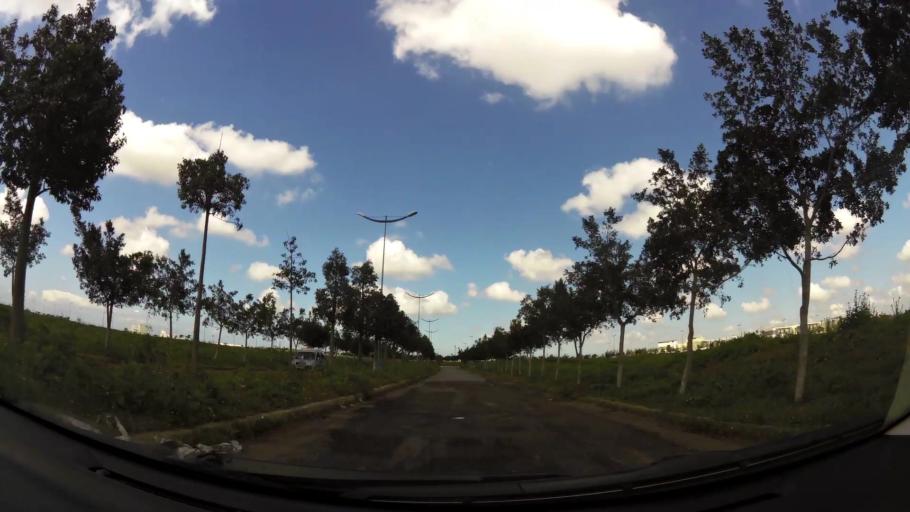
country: MA
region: Grand Casablanca
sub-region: Nouaceur
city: Dar Bouazza
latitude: 33.4214
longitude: -7.8258
